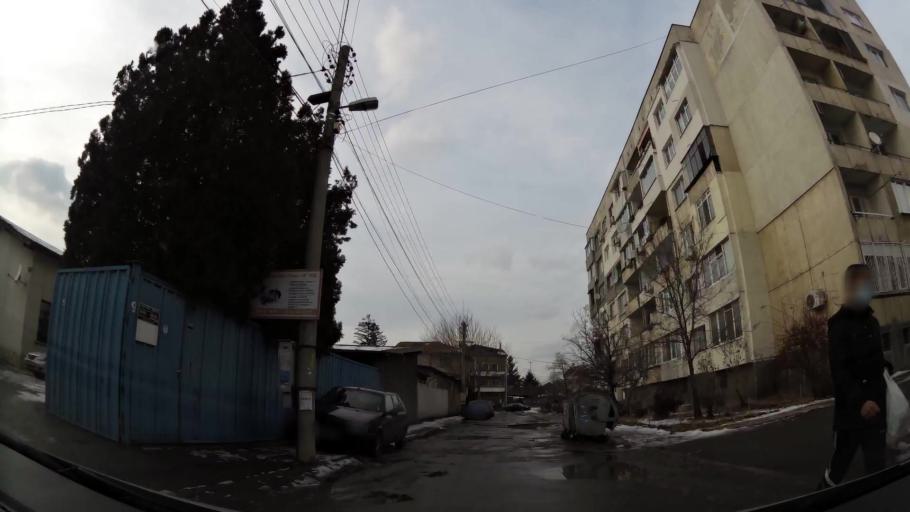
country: BG
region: Sofia-Capital
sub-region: Stolichna Obshtina
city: Sofia
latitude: 42.7139
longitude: 23.3434
